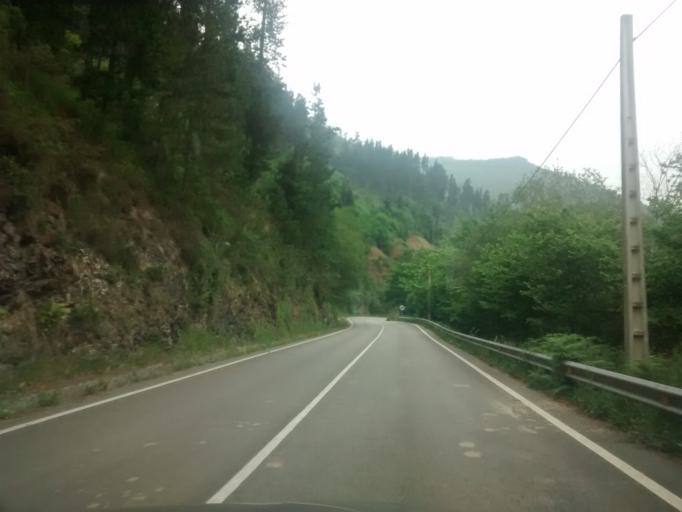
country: ES
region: Cantabria
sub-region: Provincia de Cantabria
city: Ruente
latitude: 43.1724
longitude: -4.2944
